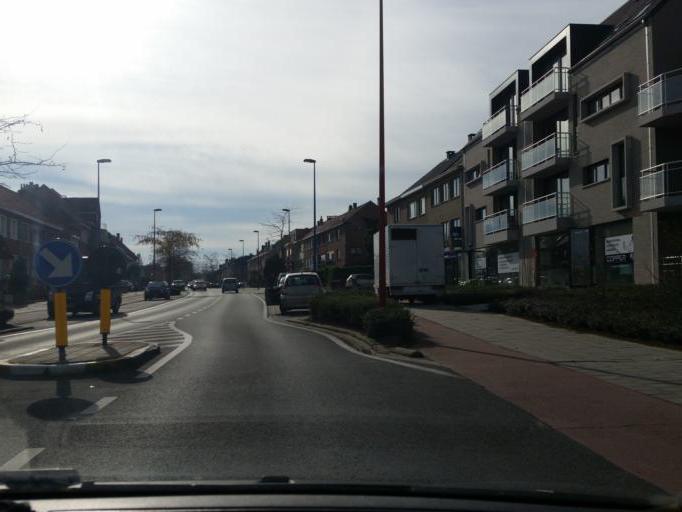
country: BE
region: Flanders
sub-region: Provincie Vlaams-Brabant
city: Grimbergen
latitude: 50.9130
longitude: 4.3669
